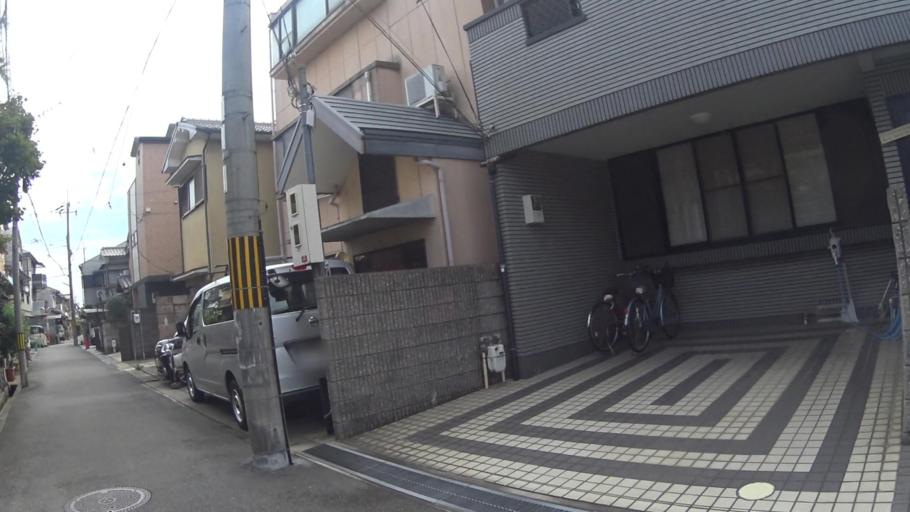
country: JP
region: Kyoto
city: Muko
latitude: 34.9501
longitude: 135.7070
